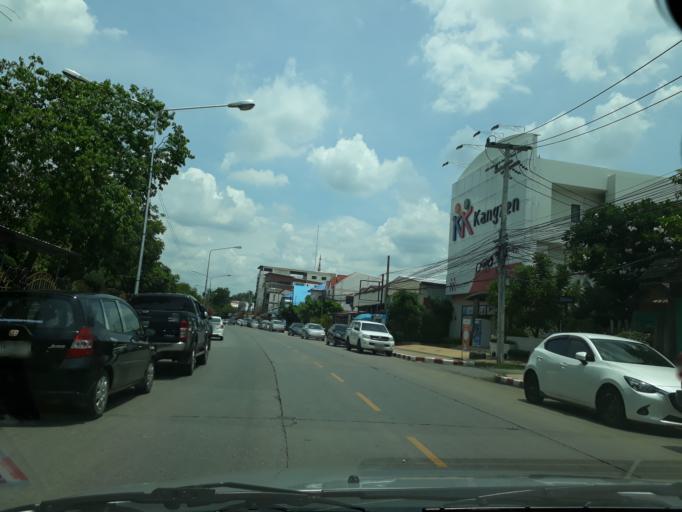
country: TH
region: Khon Kaen
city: Khon Kaen
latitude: 16.4125
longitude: 102.8351
